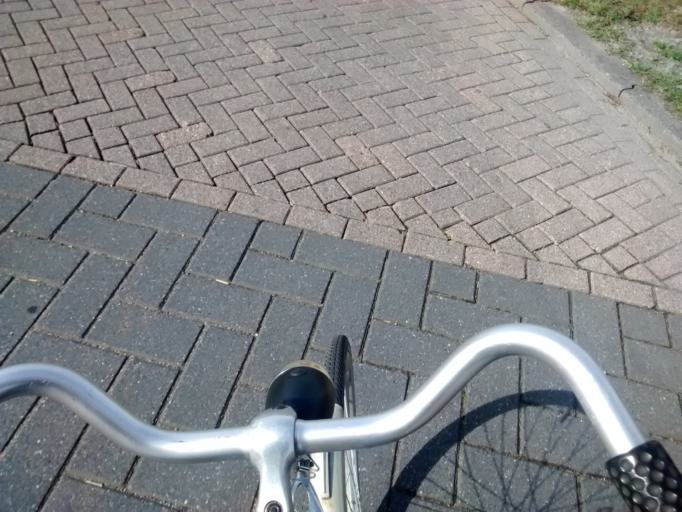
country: NL
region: Utrecht
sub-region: Gemeente Nieuwegein
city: Nieuwegein
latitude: 52.0210
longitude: 5.1019
